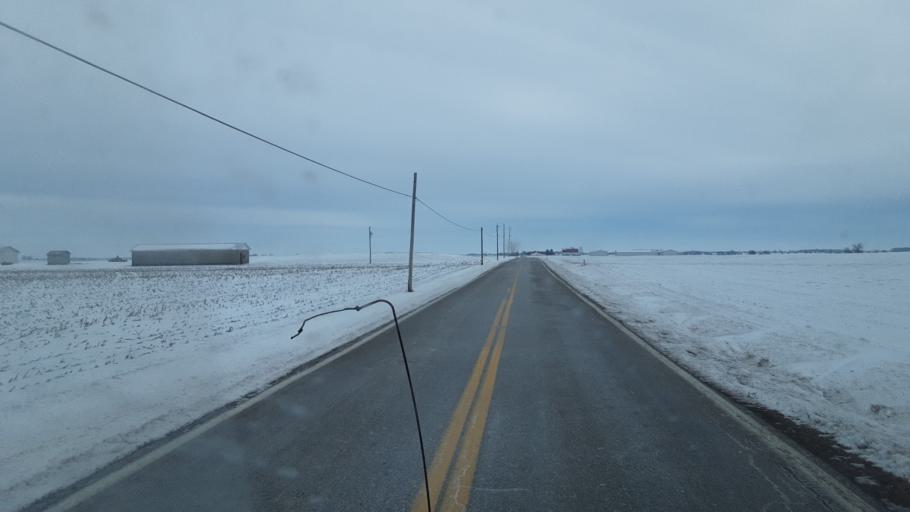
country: US
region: Ohio
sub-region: Madison County
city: Bethel
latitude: 39.7329
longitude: -83.4599
